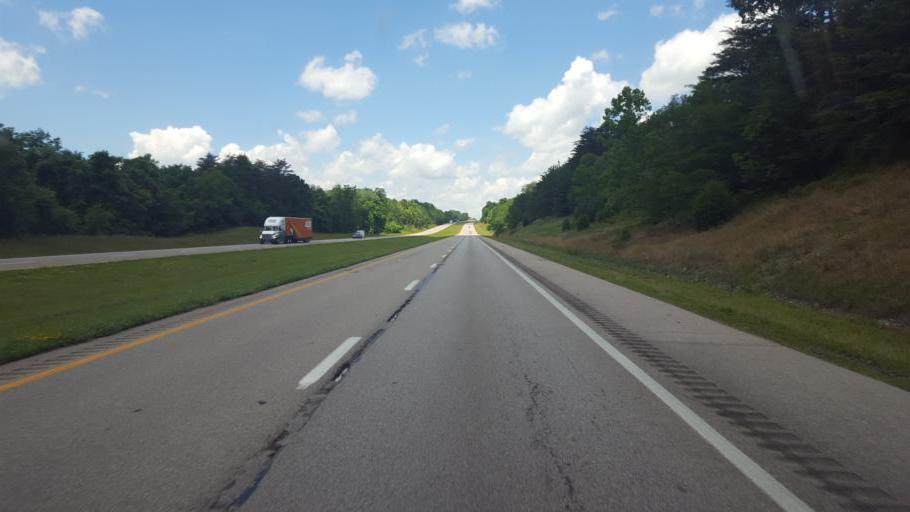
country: US
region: Ohio
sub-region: Gallia County
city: Gallipolis
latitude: 38.8664
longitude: -82.2666
